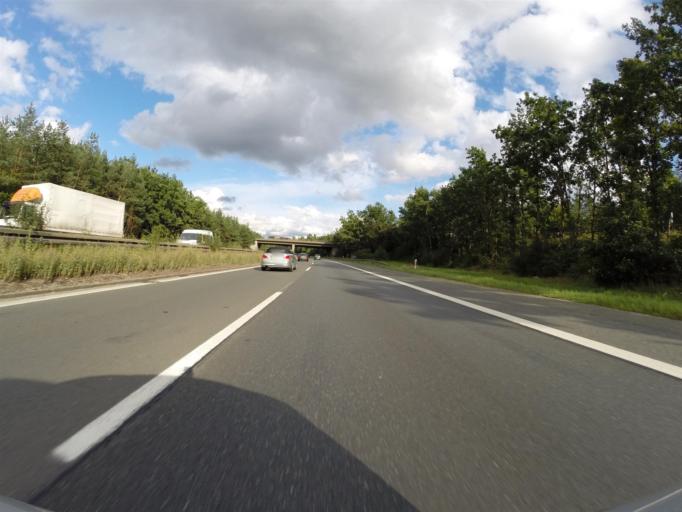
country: DE
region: Bavaria
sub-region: Regierungsbezirk Mittelfranken
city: Nuernberg
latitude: 49.3953
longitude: 11.0819
